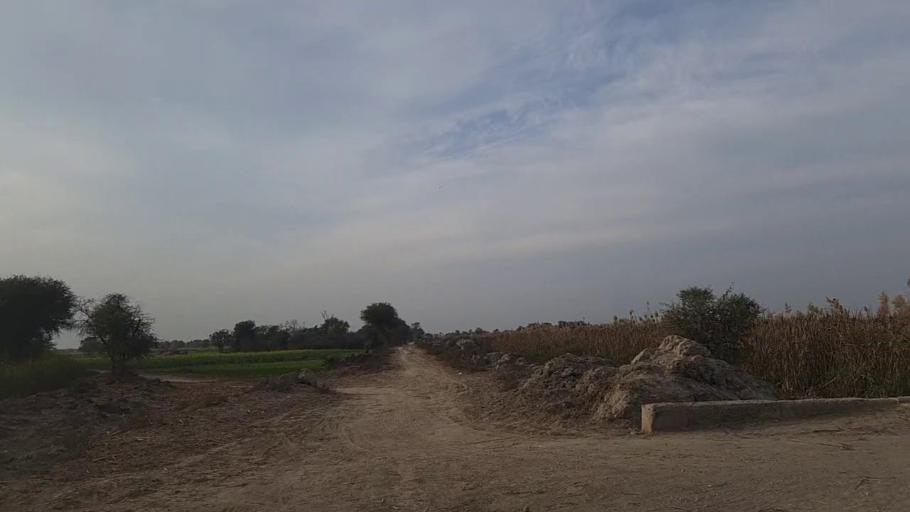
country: PK
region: Sindh
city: Daur
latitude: 26.5268
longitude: 68.4057
